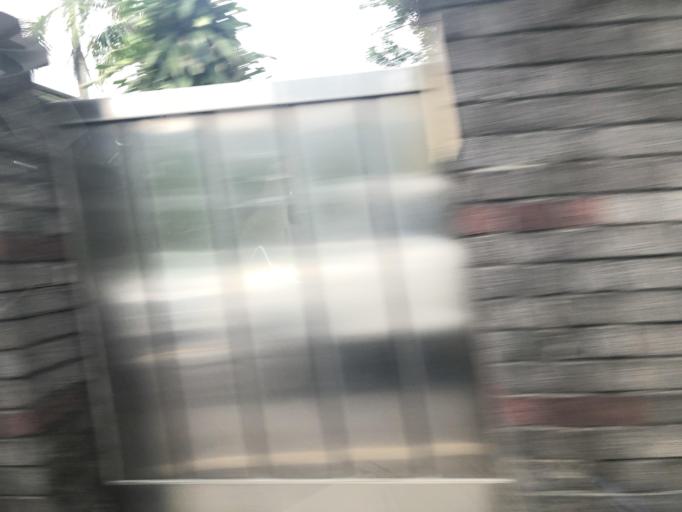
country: TW
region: Taiwan
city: Daxi
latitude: 24.9091
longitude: 121.3946
